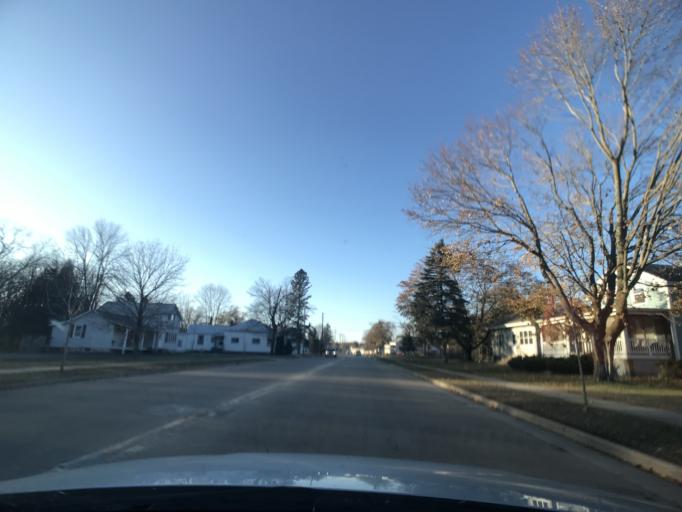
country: US
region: Wisconsin
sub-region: Oconto County
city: Oconto
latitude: 44.8912
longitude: -87.8792
